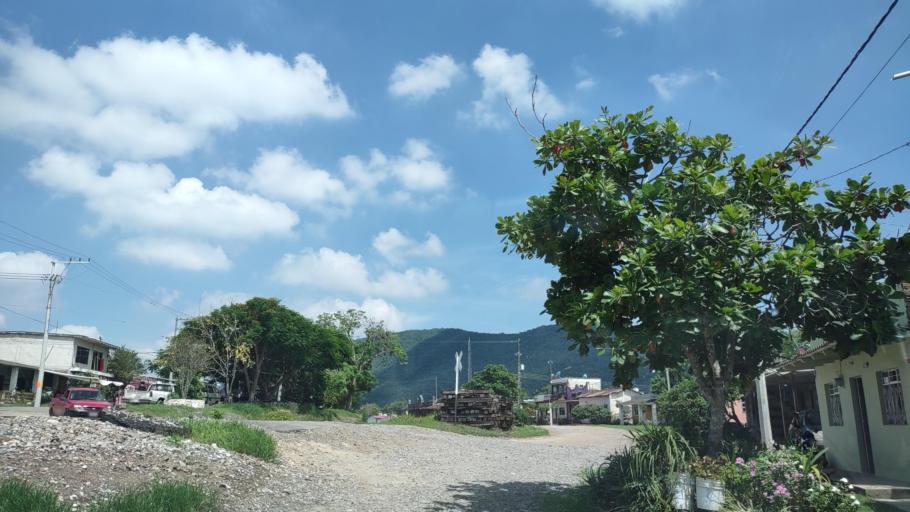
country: MX
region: Veracruz
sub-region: Coatepec
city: Bella Esperanza
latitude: 19.4291
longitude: -96.8108
